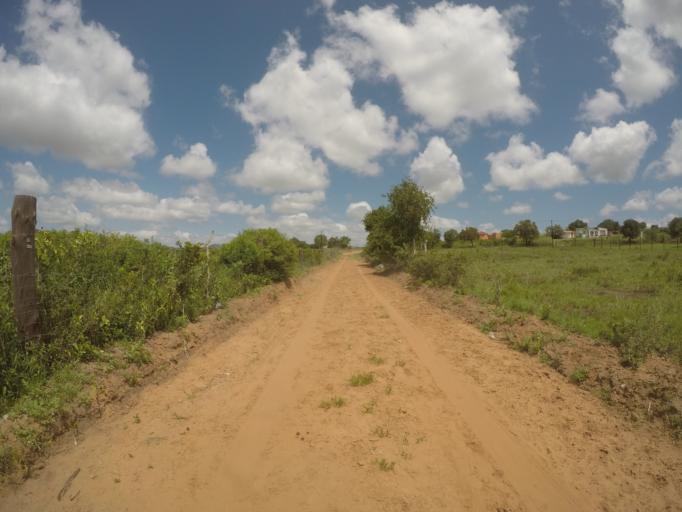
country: ZA
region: KwaZulu-Natal
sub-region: uThungulu District Municipality
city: Empangeni
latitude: -28.5850
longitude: 31.8422
